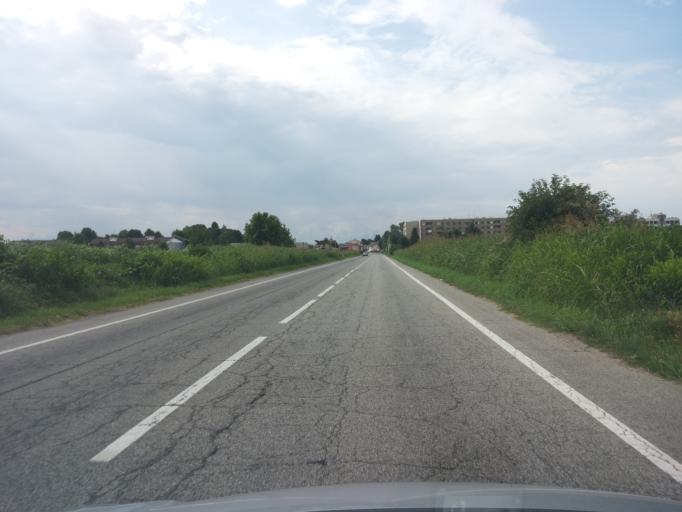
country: IT
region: Piedmont
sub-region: Provincia di Vercelli
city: Prarolo
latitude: 45.2989
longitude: 8.4494
